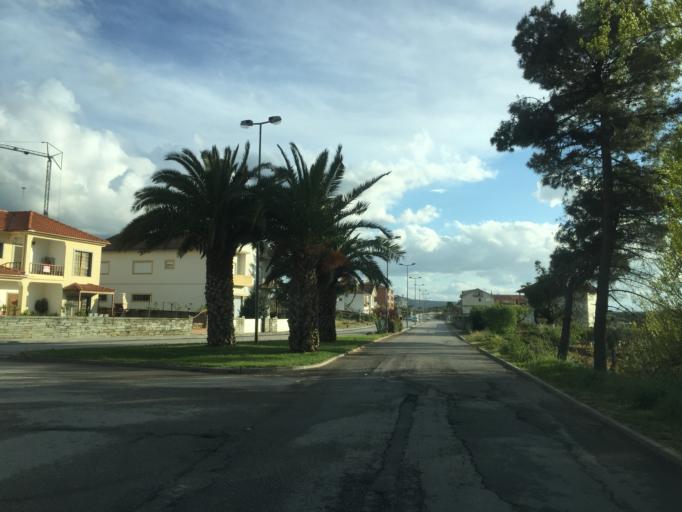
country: PT
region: Braganca
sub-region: Alfandega da Fe
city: Alfandega da Fe
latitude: 41.3376
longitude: -6.9623
